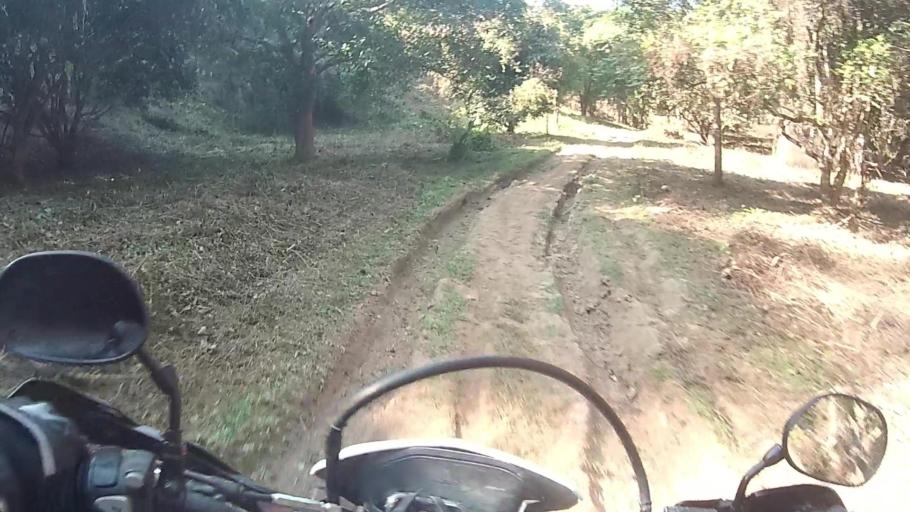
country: TH
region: Chiang Mai
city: Mae On
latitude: 18.9312
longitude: 99.2027
